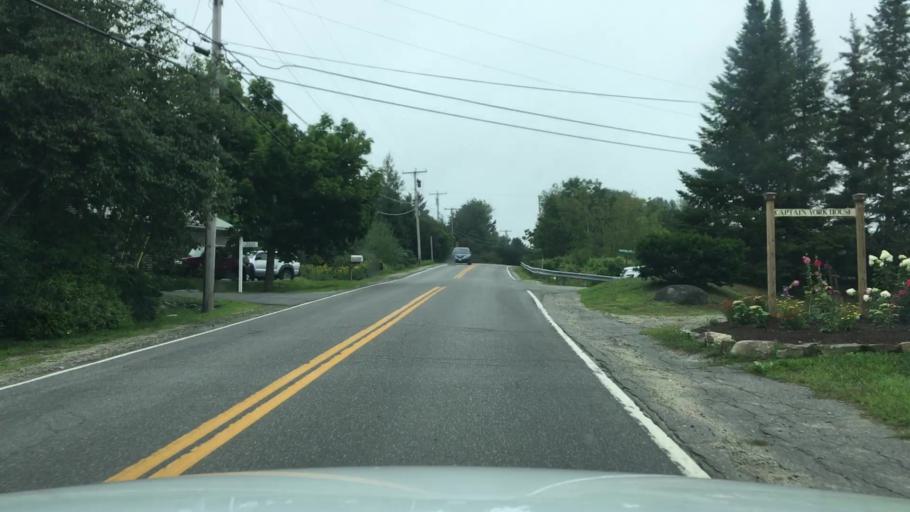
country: US
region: Maine
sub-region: Cumberland County
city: Harpswell Center
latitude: 43.7445
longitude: -69.9919
